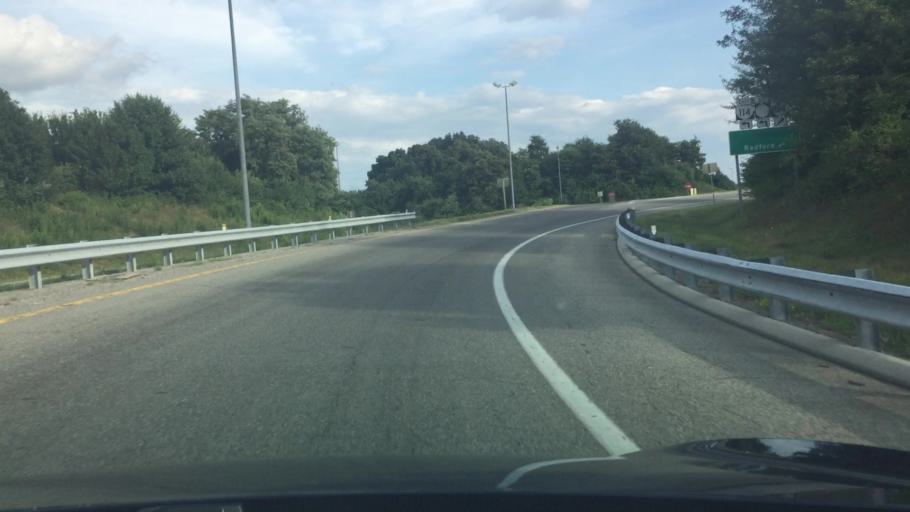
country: US
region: Virginia
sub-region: Montgomery County
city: Merrimac
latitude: 37.1665
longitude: -80.4130
